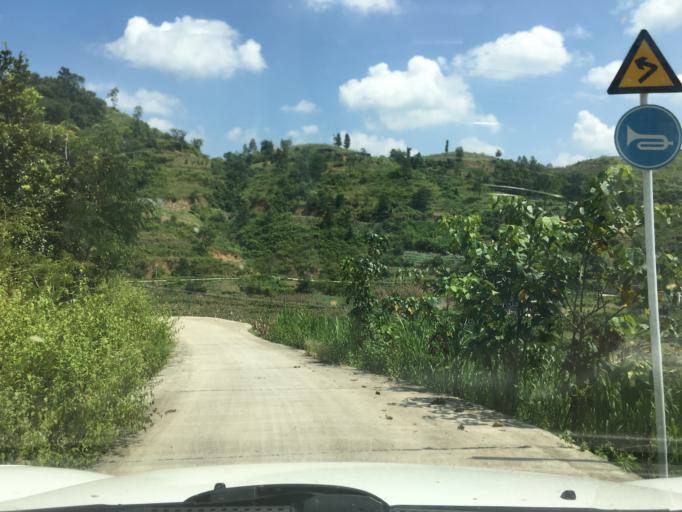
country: CN
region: Guangxi Zhuangzu Zizhiqu
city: Xinzhou
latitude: 25.4591
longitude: 105.7706
